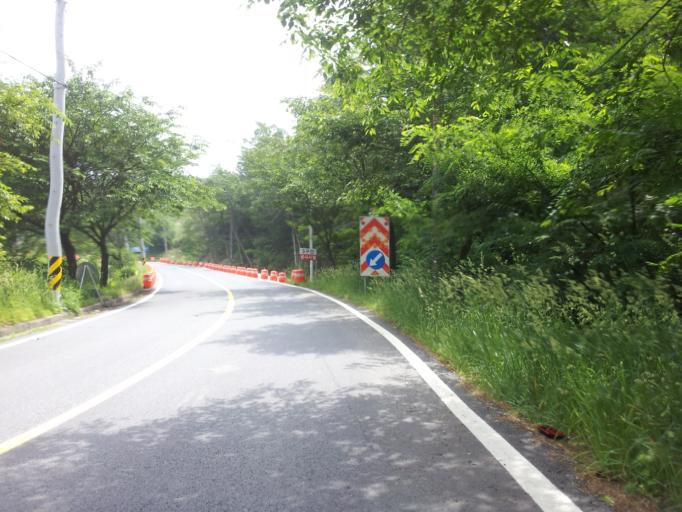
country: KR
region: Chungcheongbuk-do
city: Okcheon
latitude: 36.3816
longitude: 127.5175
